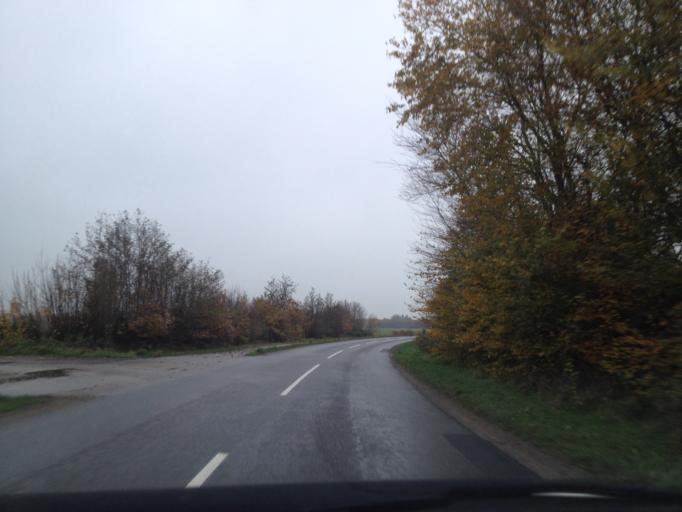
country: DK
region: South Denmark
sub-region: Tonder Kommune
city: Sherrebek
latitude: 55.1176
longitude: 8.7545
